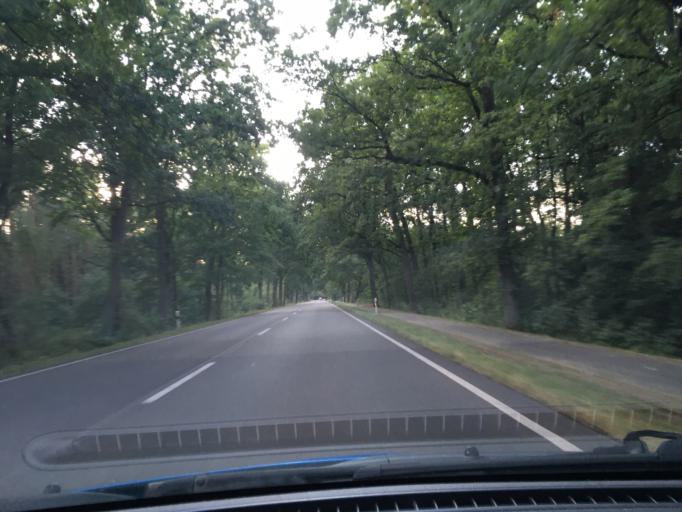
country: DE
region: Lower Saxony
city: Hambuhren
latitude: 52.6801
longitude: 10.0095
